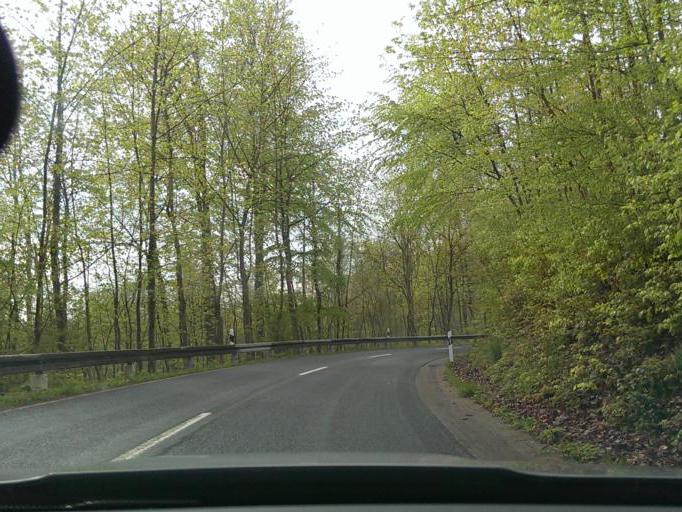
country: DE
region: Lower Saxony
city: Nordstemmen
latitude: 52.1773
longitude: 9.7654
